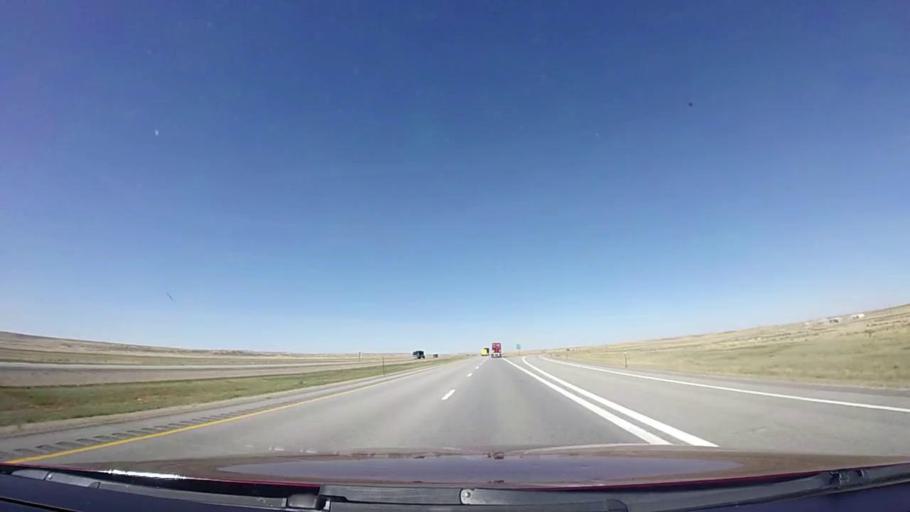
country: US
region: Wyoming
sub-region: Carbon County
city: Rawlins
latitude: 41.6663
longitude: -108.0264
